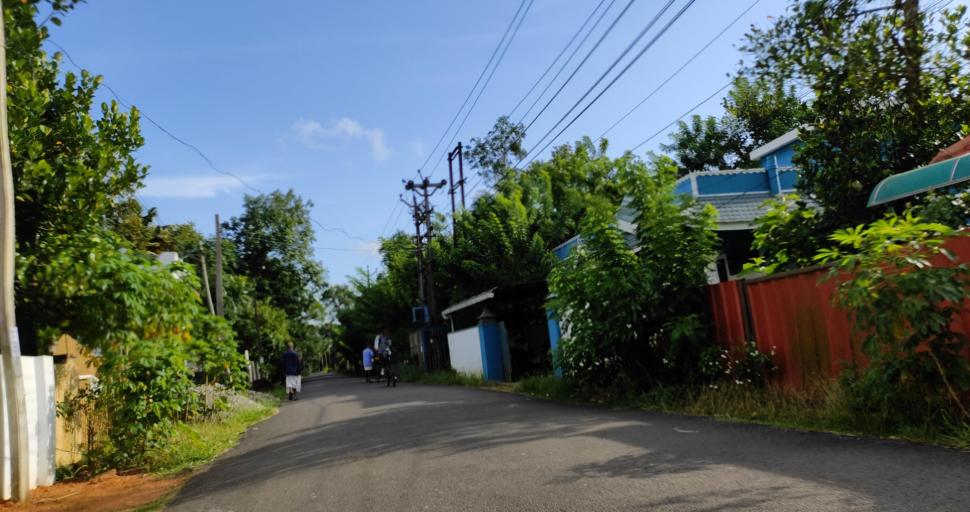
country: IN
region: Kerala
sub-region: Alappuzha
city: Shertallai
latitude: 9.6197
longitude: 76.3418
